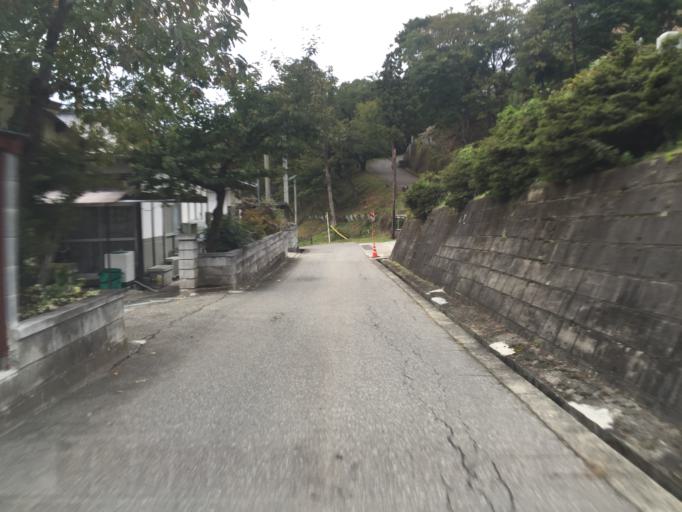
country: JP
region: Fukushima
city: Kitakata
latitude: 37.4824
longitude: 139.9483
